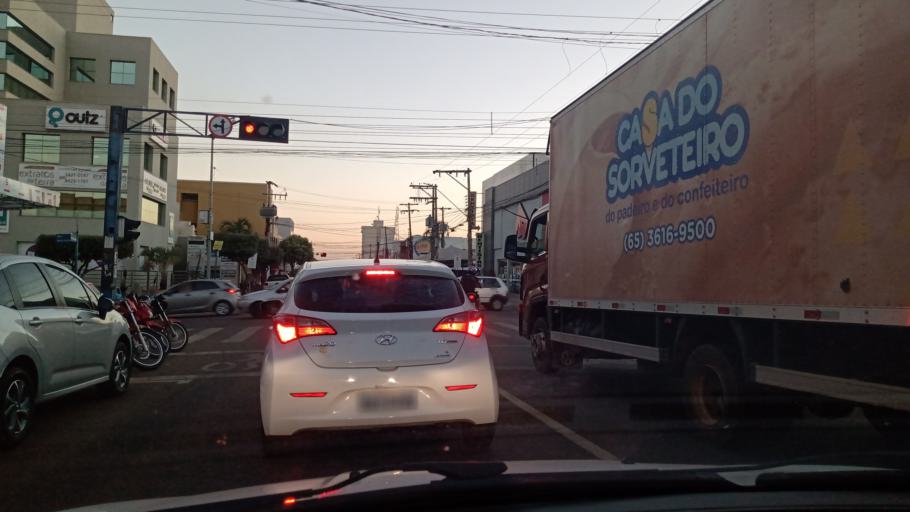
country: BR
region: Mato Grosso
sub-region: Rondonopolis
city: Rondonopolis
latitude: -16.4684
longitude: -54.6290
